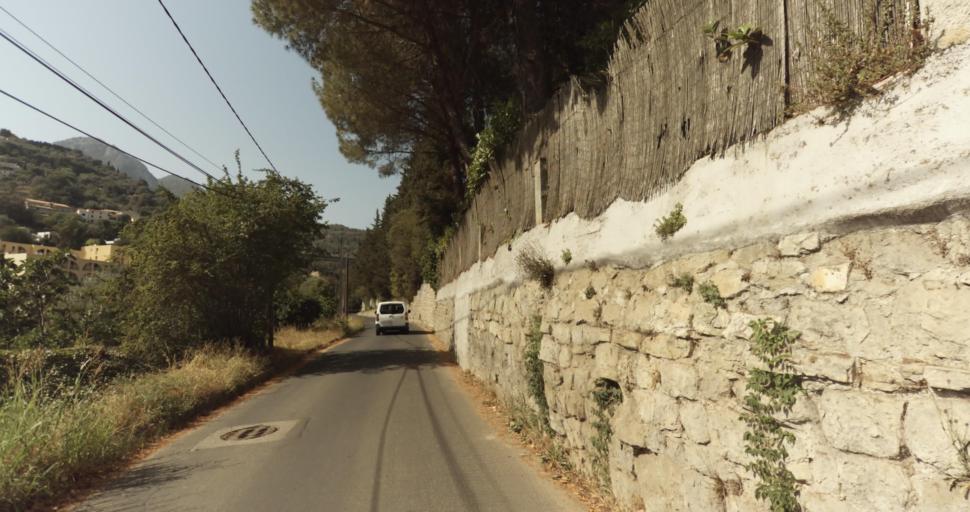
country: FR
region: Provence-Alpes-Cote d'Azur
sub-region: Departement des Alpes-Maritimes
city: Sainte-Agnes
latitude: 43.7926
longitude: 7.4799
